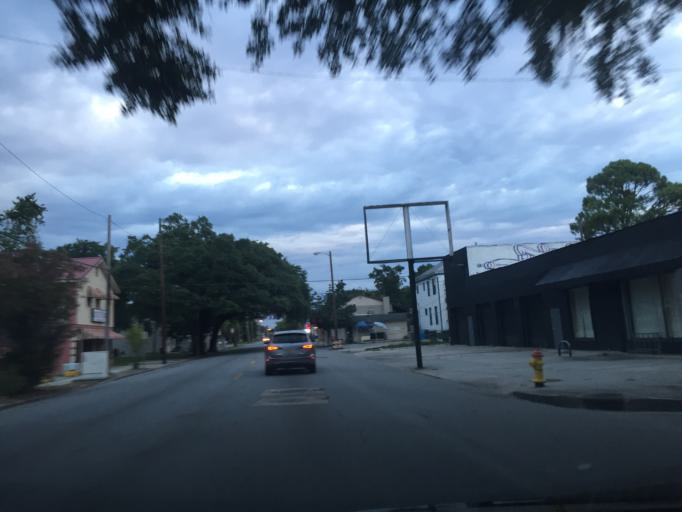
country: US
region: Georgia
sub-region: Chatham County
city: Savannah
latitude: 32.0590
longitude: -81.1040
